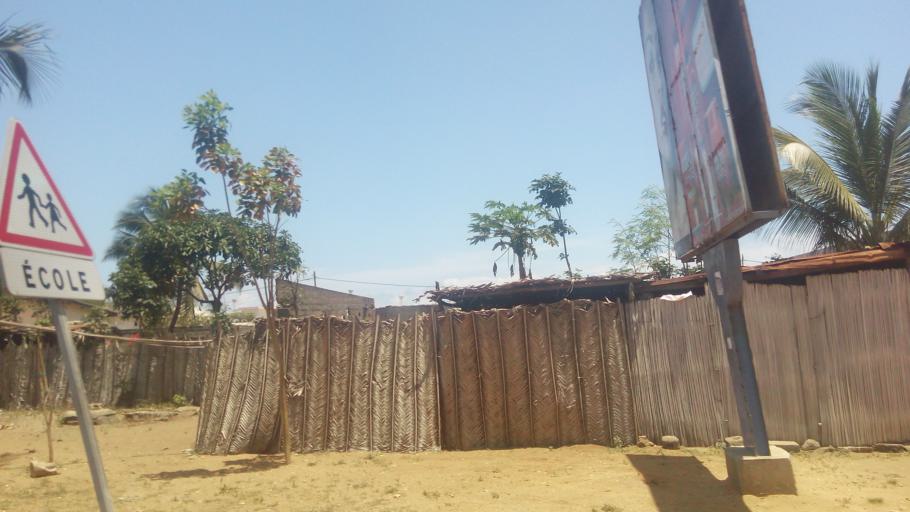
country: BJ
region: Mono
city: Grand-Popo
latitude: 6.2752
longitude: 1.8022
